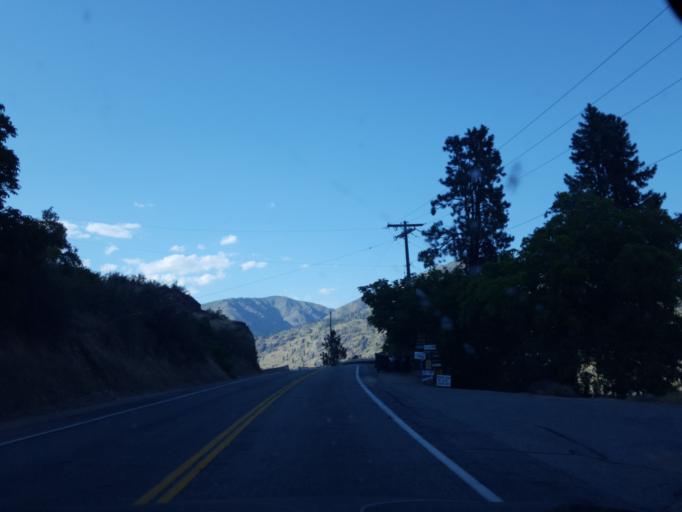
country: US
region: Washington
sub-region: Chelan County
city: Granite Falls
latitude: 47.9583
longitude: -120.2097
